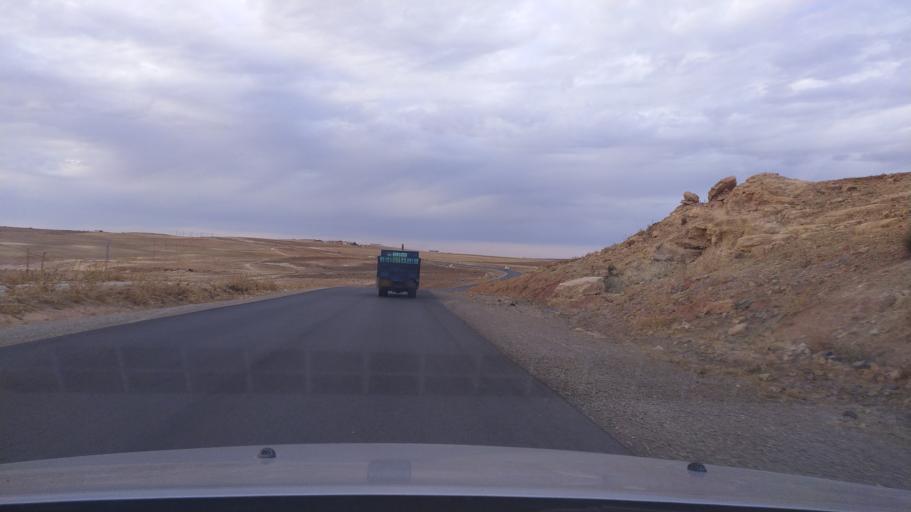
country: DZ
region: Tiaret
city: Frenda
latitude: 34.9947
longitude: 1.1281
